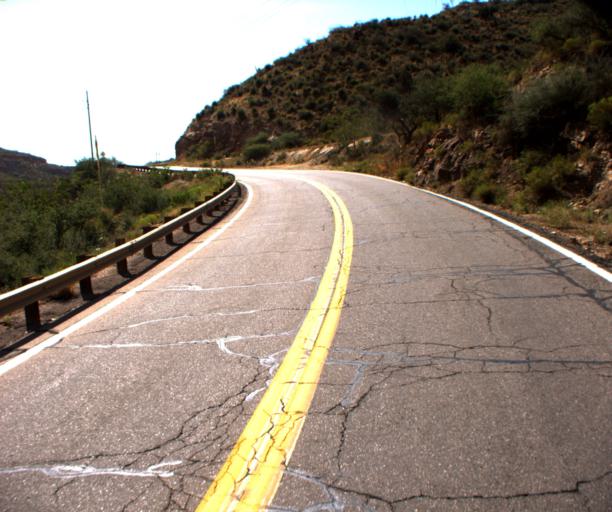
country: US
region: Arizona
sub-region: Greenlee County
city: Morenci
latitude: 33.0739
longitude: -109.3609
